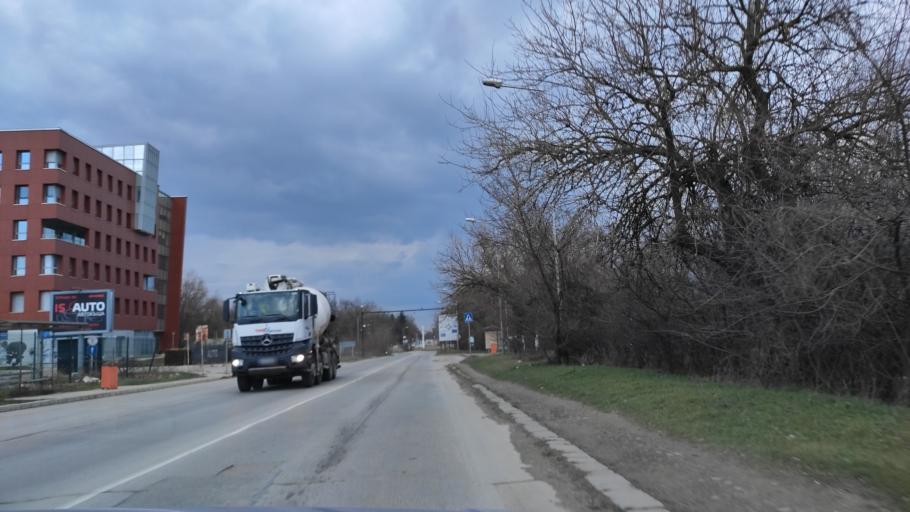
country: BG
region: Varna
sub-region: Obshtina Aksakovo
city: Aksakovo
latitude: 43.2265
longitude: 27.8560
